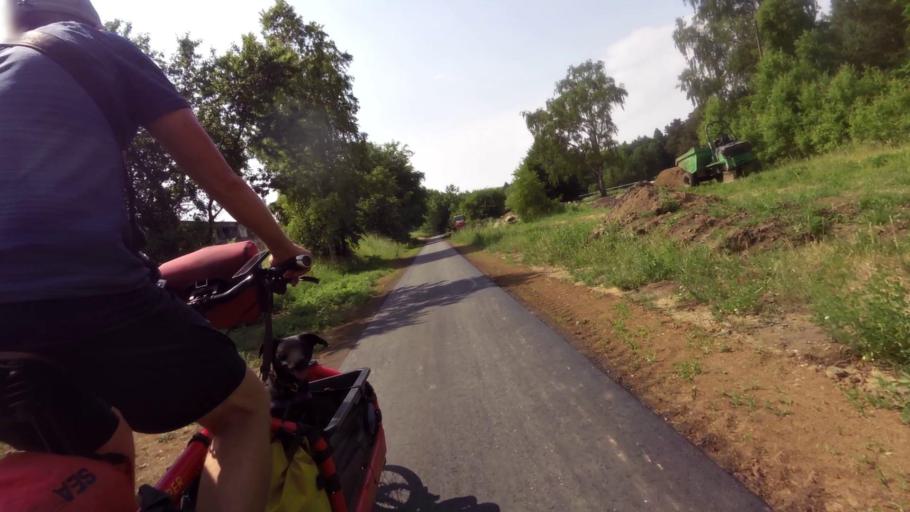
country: PL
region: West Pomeranian Voivodeship
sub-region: Powiat gryfinski
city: Gryfino
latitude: 53.2185
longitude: 14.6027
